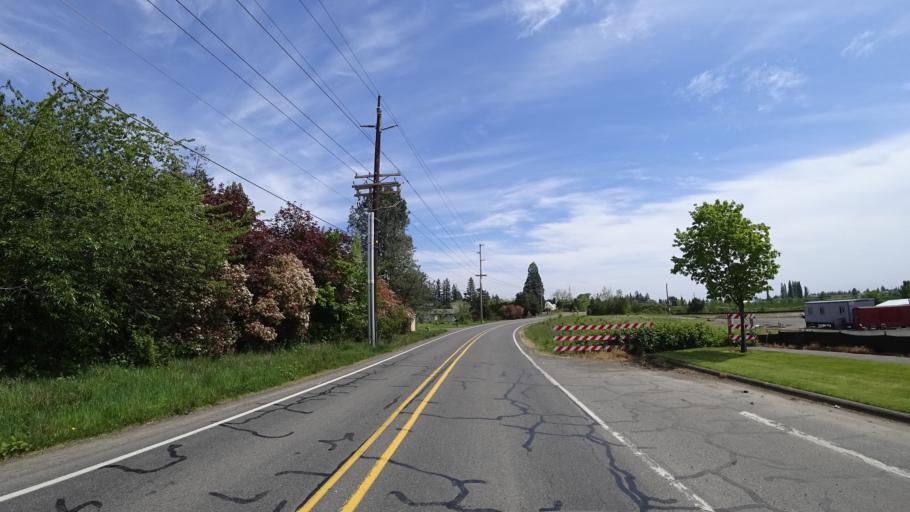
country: US
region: Oregon
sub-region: Washington County
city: Rockcreek
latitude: 45.5731
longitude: -122.9046
